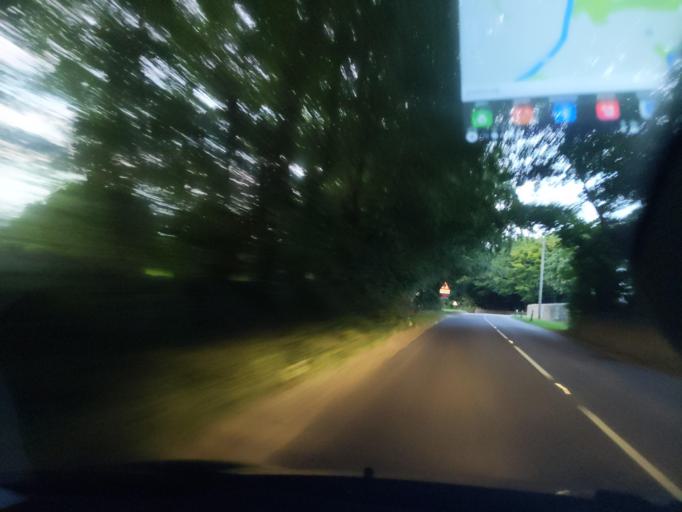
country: GB
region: England
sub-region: Cornwall
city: Camborne
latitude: 50.1977
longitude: -5.3060
